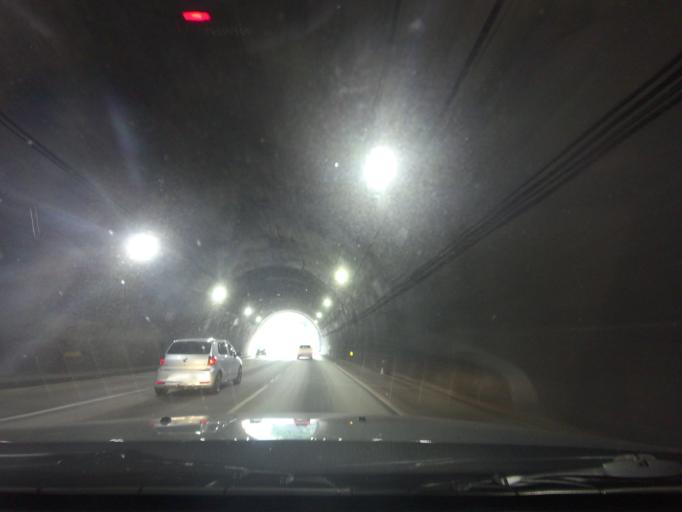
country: BR
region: Sao Paulo
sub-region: Cubatao
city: Cubatao
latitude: -23.9083
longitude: -46.5142
